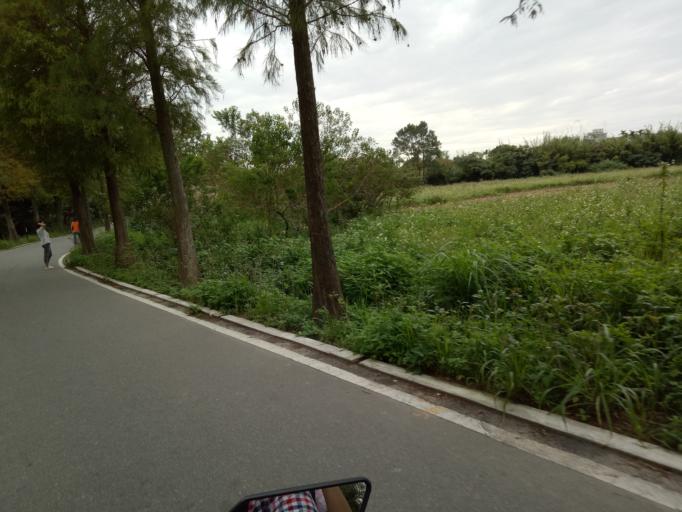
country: TW
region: Taiwan
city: Daxi
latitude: 24.8720
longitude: 121.2557
